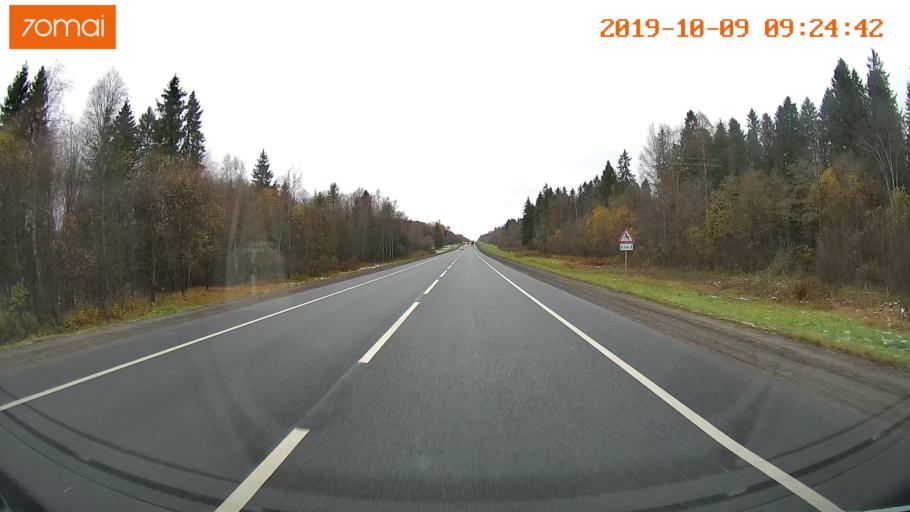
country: RU
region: Vologda
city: Vologda
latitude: 59.0820
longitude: 40.0122
